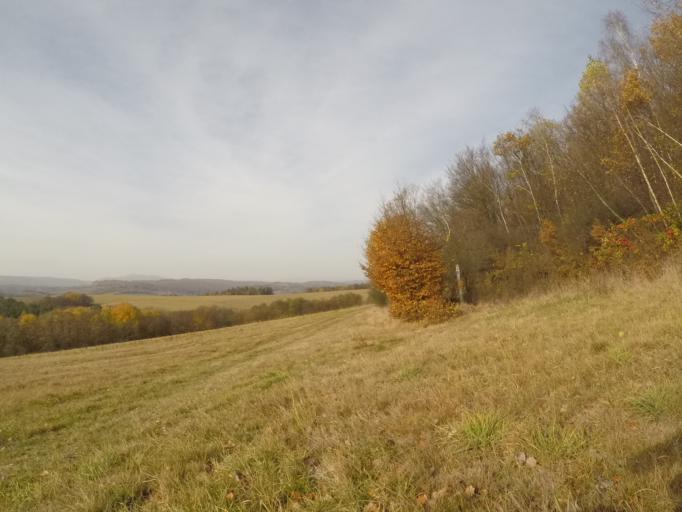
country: SK
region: Presovsky
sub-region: Okres Presov
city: Presov
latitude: 48.9231
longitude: 21.2210
